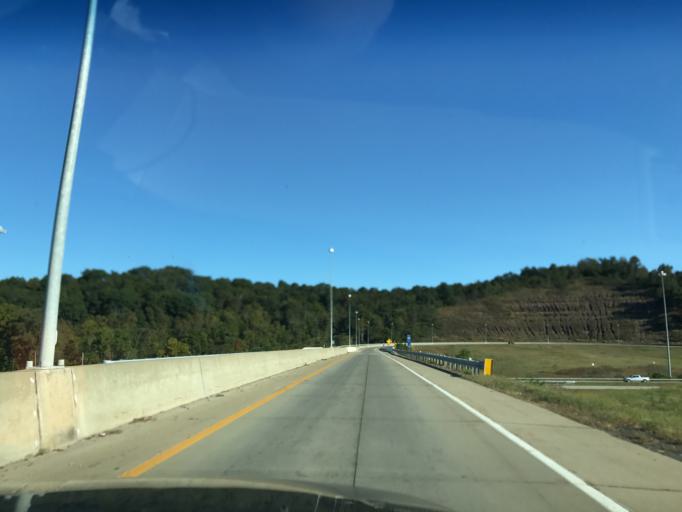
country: US
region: West Virginia
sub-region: Wood County
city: Blennerhassett
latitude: 39.2829
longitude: -81.6471
